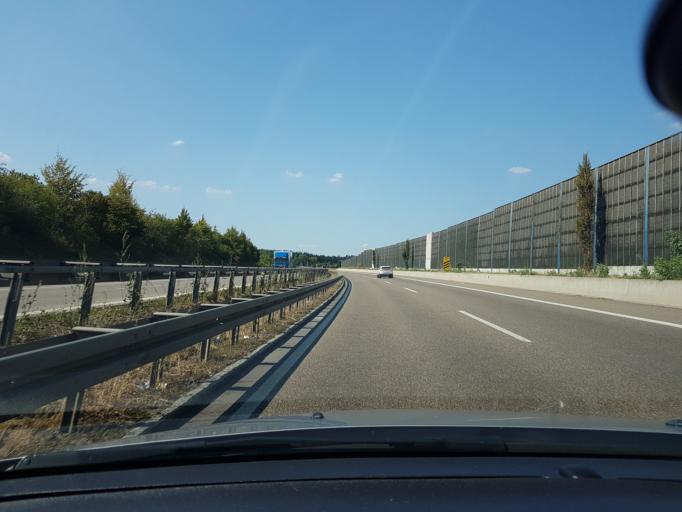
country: DE
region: Bavaria
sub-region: Swabia
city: Langweid
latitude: 48.4983
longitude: 10.8602
